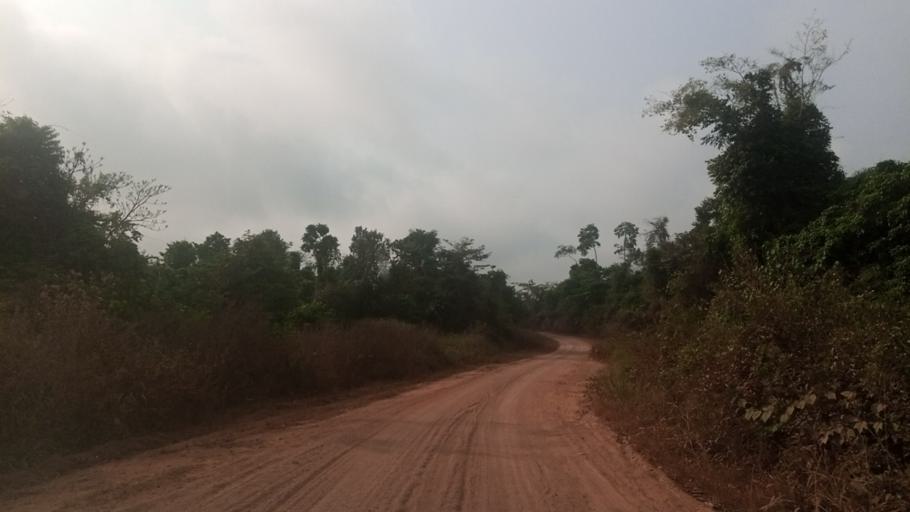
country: NG
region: Osun
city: Modakeke
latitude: 7.1231
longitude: 4.4086
